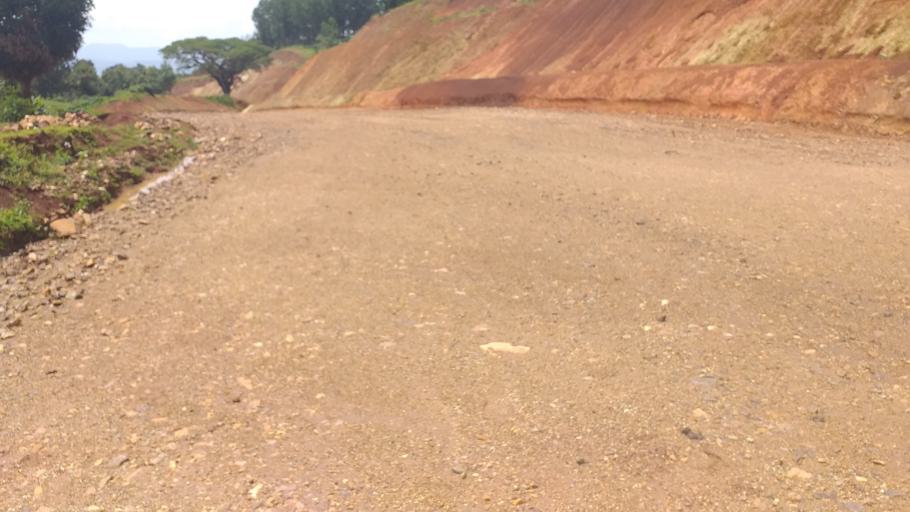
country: ET
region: Southern Nations, Nationalities, and People's Region
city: Bako
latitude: 5.9821
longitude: 36.5282
